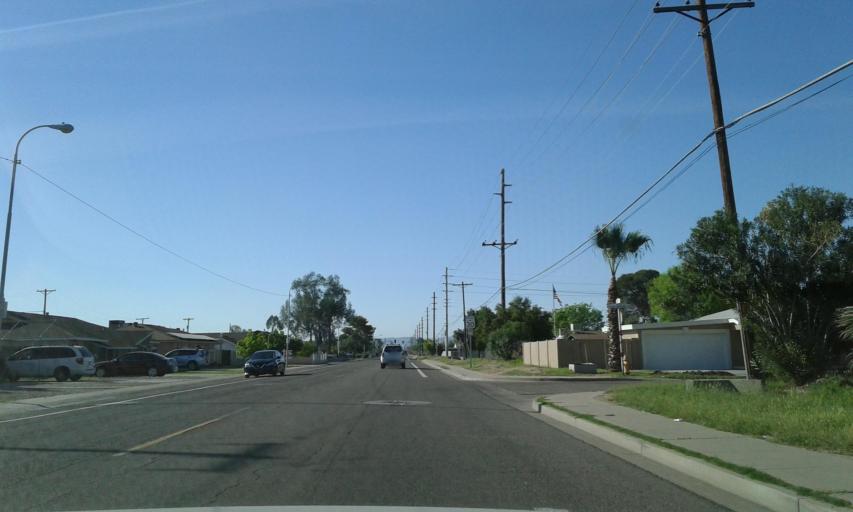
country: US
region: Arizona
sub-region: Maricopa County
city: Phoenix
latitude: 33.5199
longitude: -112.1084
